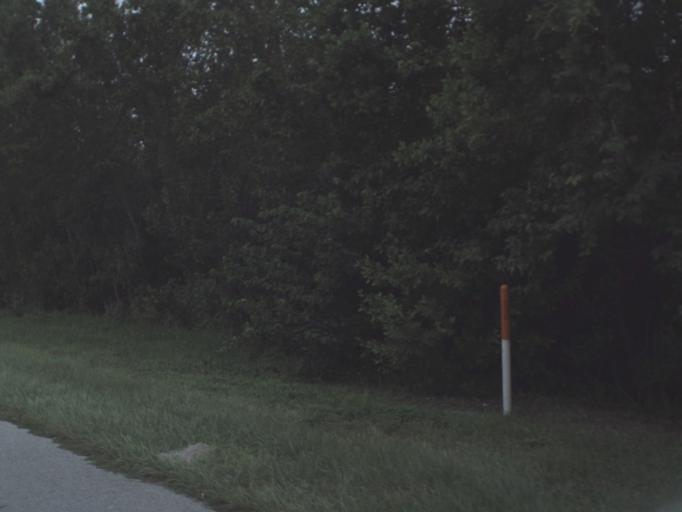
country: US
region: Florida
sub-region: Collier County
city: Marco
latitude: 25.9684
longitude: -81.7081
